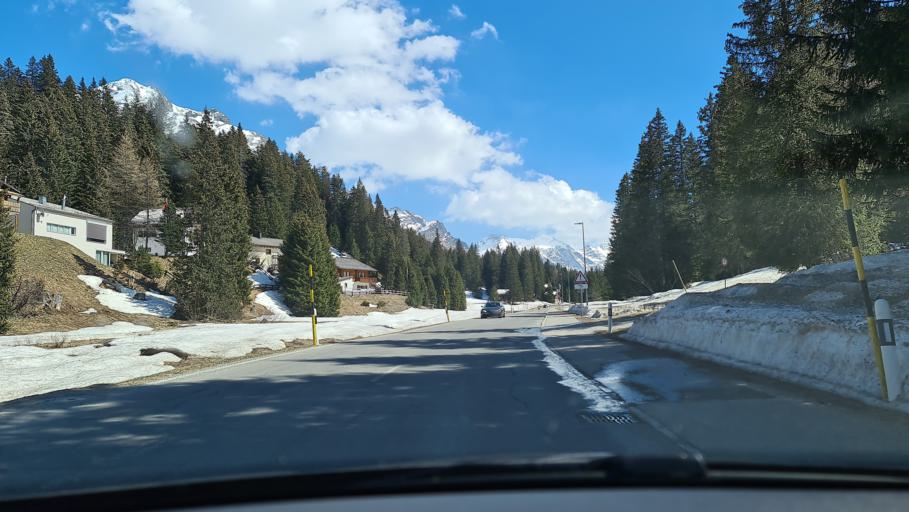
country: CH
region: Grisons
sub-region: Hinterrhein District
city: Hinterrhein
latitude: 46.4576
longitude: 9.1954
